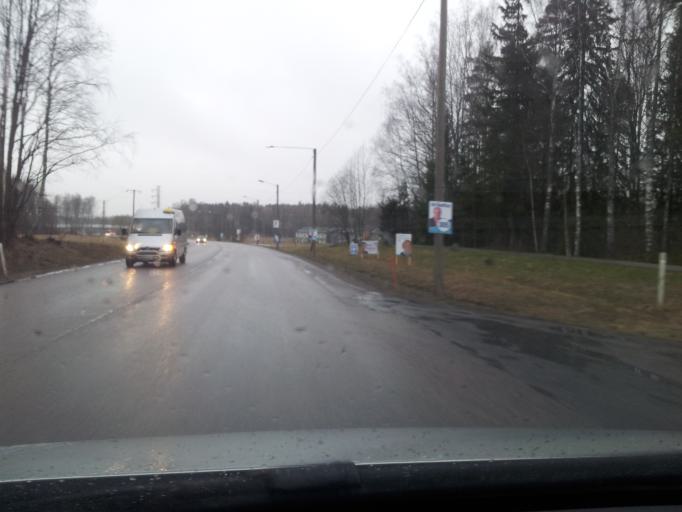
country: FI
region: Uusimaa
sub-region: Helsinki
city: Espoo
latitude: 60.1648
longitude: 24.6258
